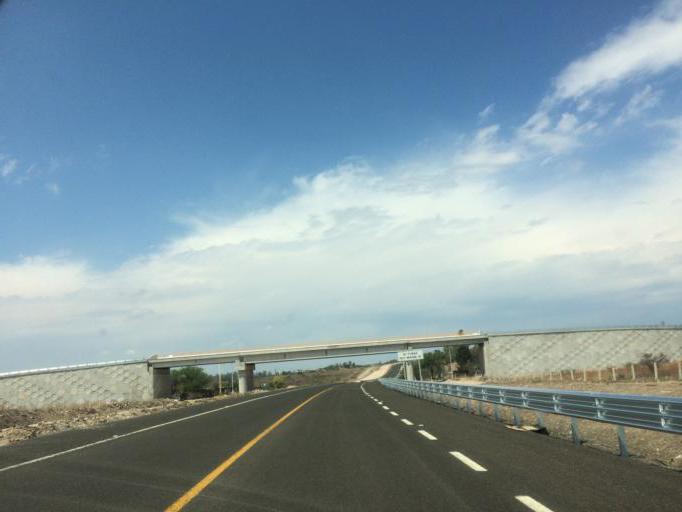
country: MX
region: Guanajuato
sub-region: Silao de la Victoria
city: El Refugio de los Sauces
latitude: 21.0334
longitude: -101.5047
